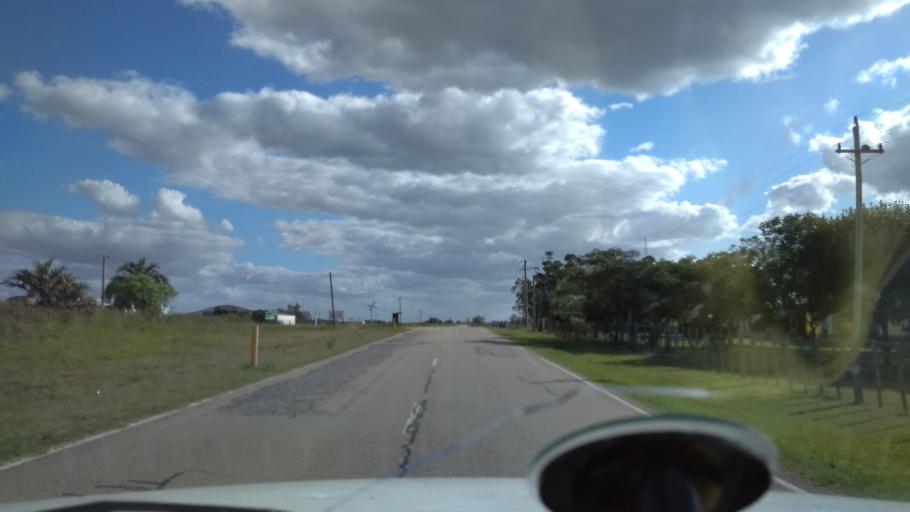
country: UY
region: Florida
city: Casupa
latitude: -34.1488
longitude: -55.6815
